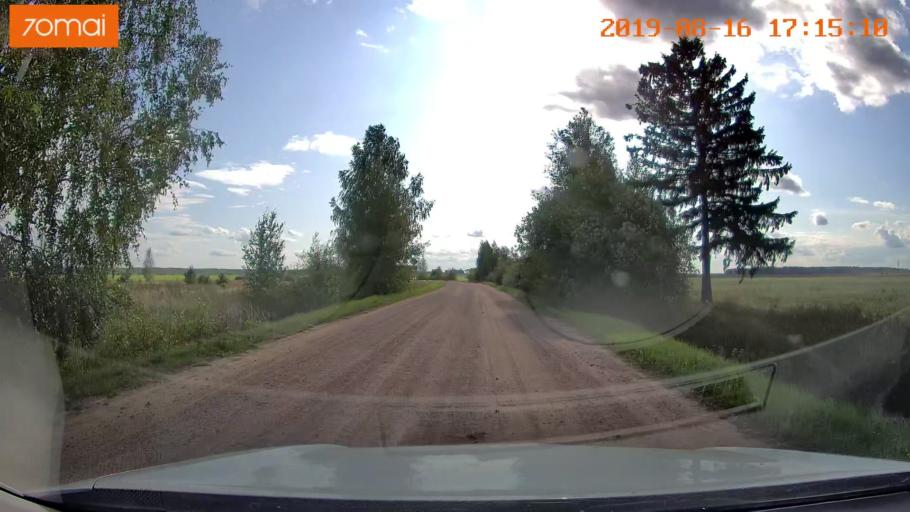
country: BY
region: Mogilev
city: Hlusha
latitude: 53.1805
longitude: 28.8471
